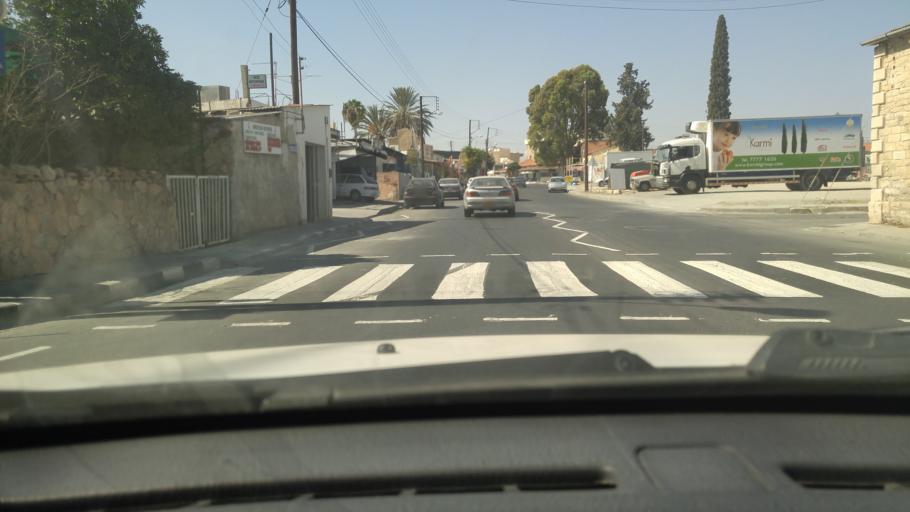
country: CY
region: Limassol
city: Limassol
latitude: 34.6737
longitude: 33.0325
